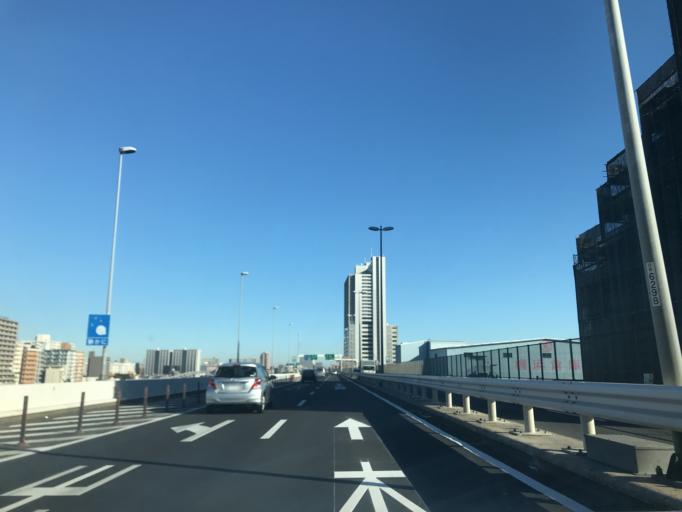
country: JP
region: Tokyo
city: Urayasu
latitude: 35.7219
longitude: 139.8098
